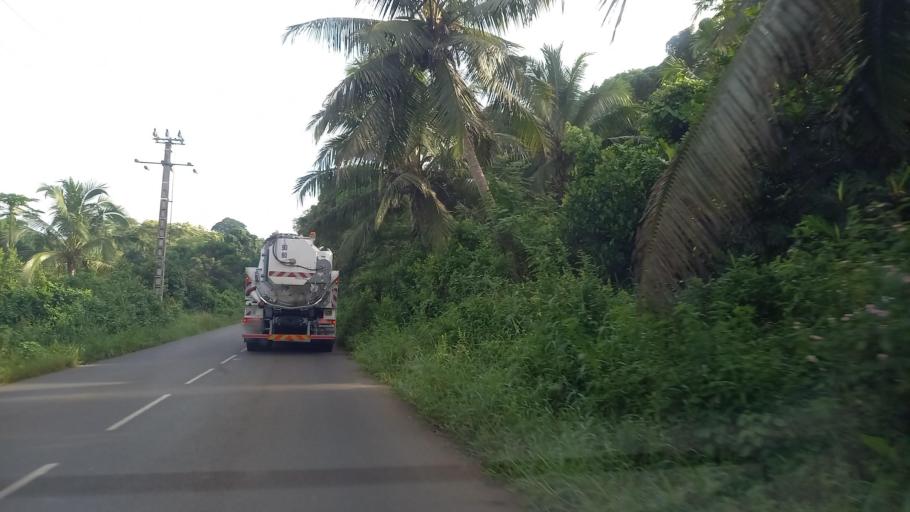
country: YT
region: Chiconi
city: Chiconi
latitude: -12.8105
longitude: 45.1271
